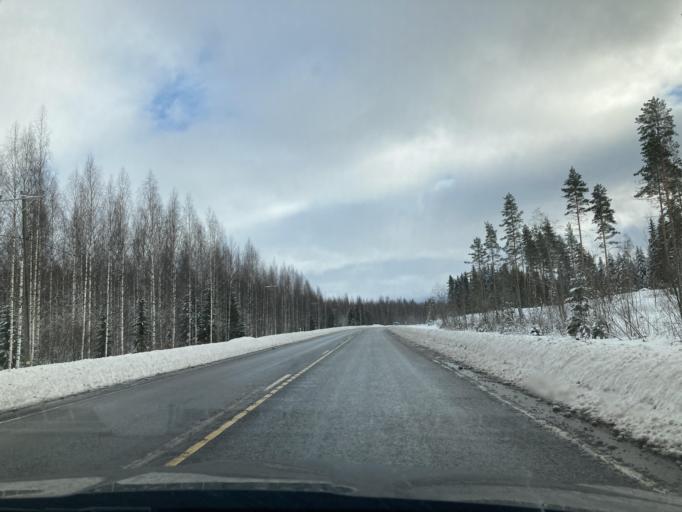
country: FI
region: Central Finland
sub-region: Jaemsae
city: Jaemsae
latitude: 61.7976
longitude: 25.2075
